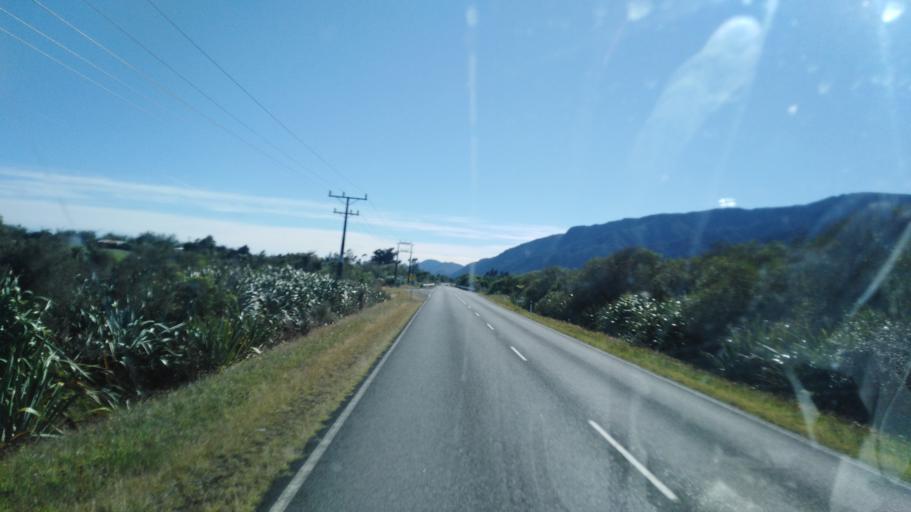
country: NZ
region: West Coast
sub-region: Buller District
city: Westport
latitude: -41.6832
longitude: 171.7897
